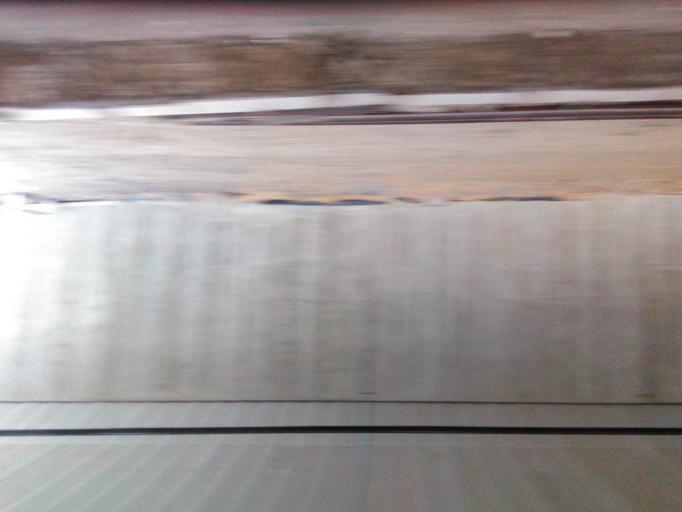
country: LU
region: Luxembourg
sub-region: Canton d'Esch-sur-Alzette
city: Bettembourg
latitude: 49.5197
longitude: 6.1023
